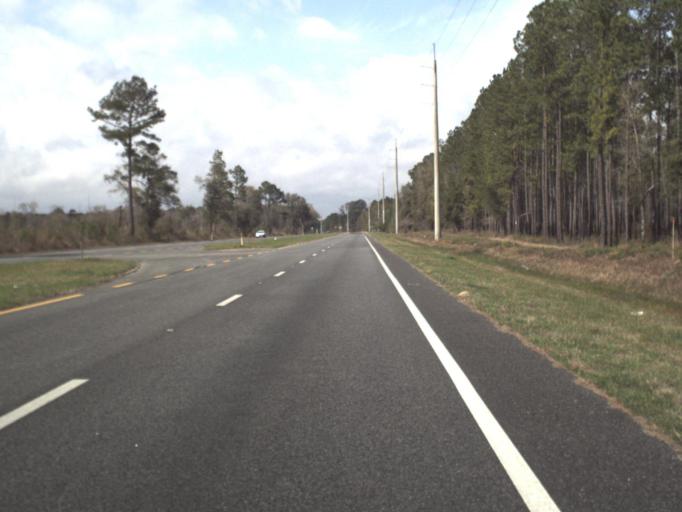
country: US
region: Florida
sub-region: Leon County
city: Tallahassee
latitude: 30.4216
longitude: -84.1055
